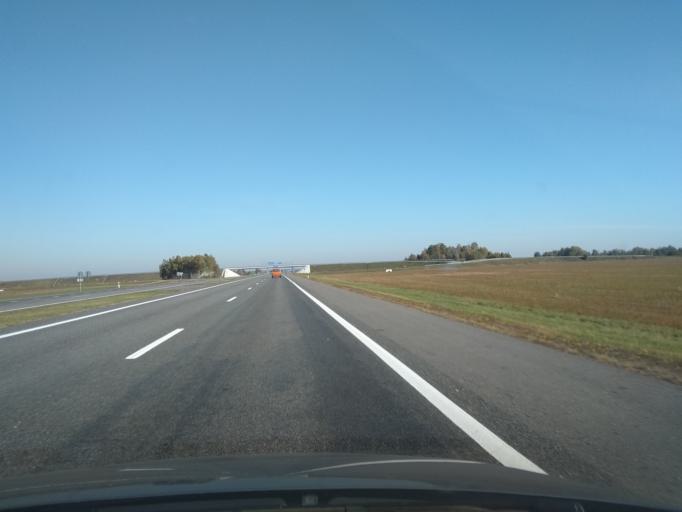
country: BY
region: Brest
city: Antopal'
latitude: 52.3039
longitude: 24.5923
